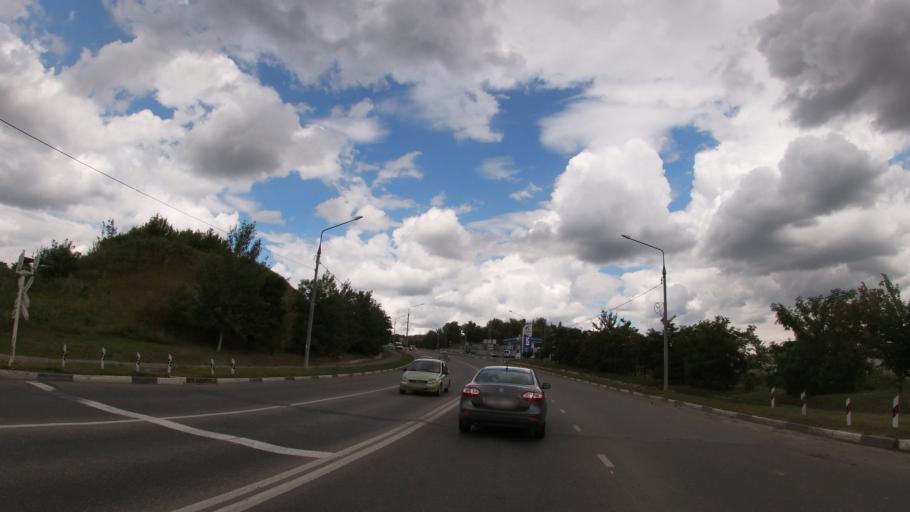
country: RU
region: Belgorod
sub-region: Belgorodskiy Rayon
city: Belgorod
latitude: 50.6089
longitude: 36.6132
